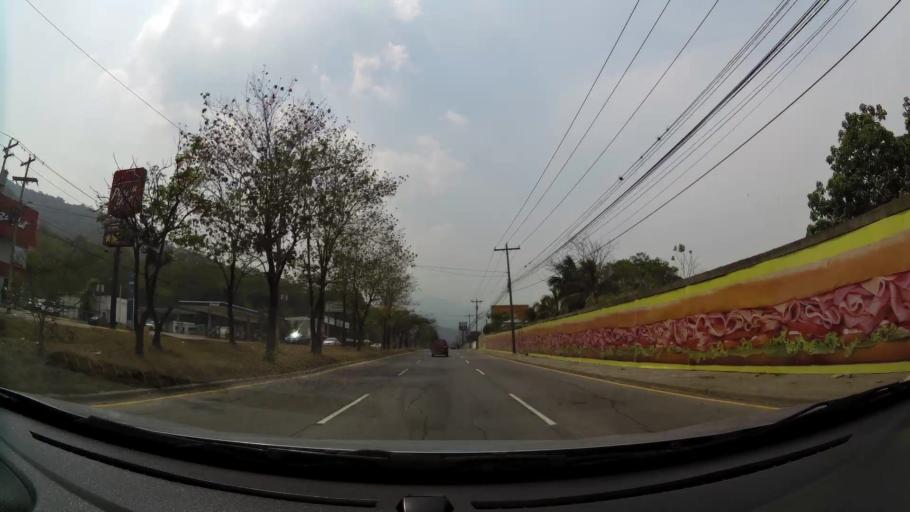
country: HN
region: Cortes
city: San Pedro Sula
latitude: 15.4559
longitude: -88.0253
